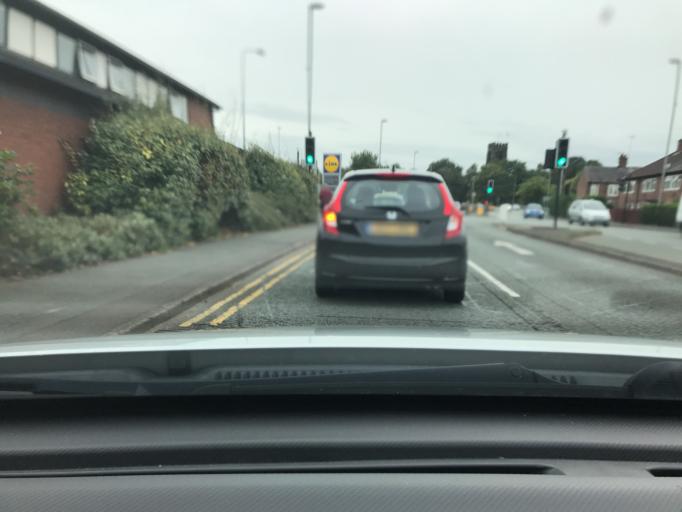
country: GB
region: England
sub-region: Cheshire West and Chester
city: Marston
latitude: 53.2612
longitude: -2.5090
